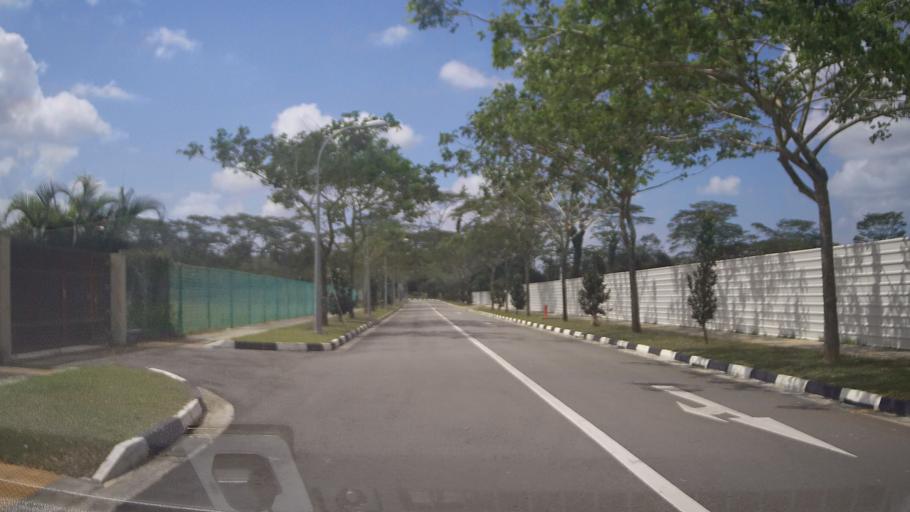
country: MY
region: Johor
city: Johor Bahru
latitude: 1.4208
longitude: 103.7223
